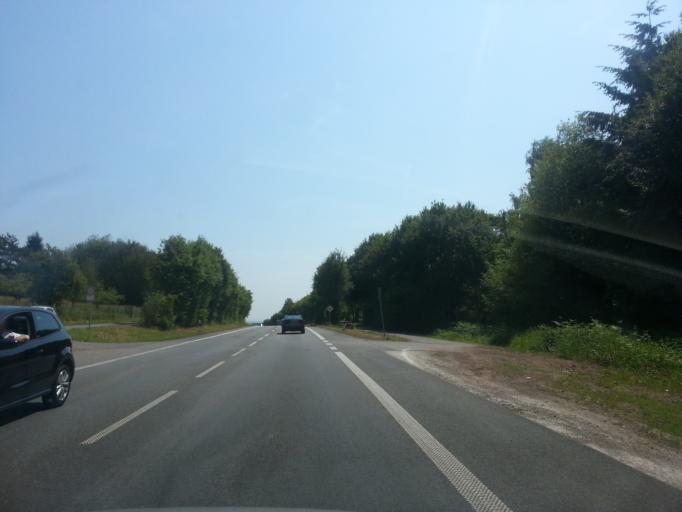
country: DE
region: Hesse
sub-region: Regierungsbezirk Darmstadt
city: Dietzenbach
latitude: 50.0023
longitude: 8.7615
